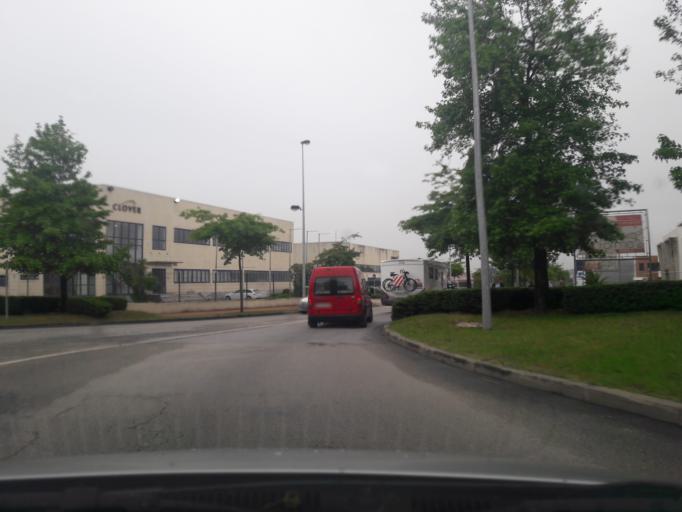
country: PT
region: Porto
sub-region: Vila do Conde
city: Arvore
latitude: 41.3300
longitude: -8.7188
